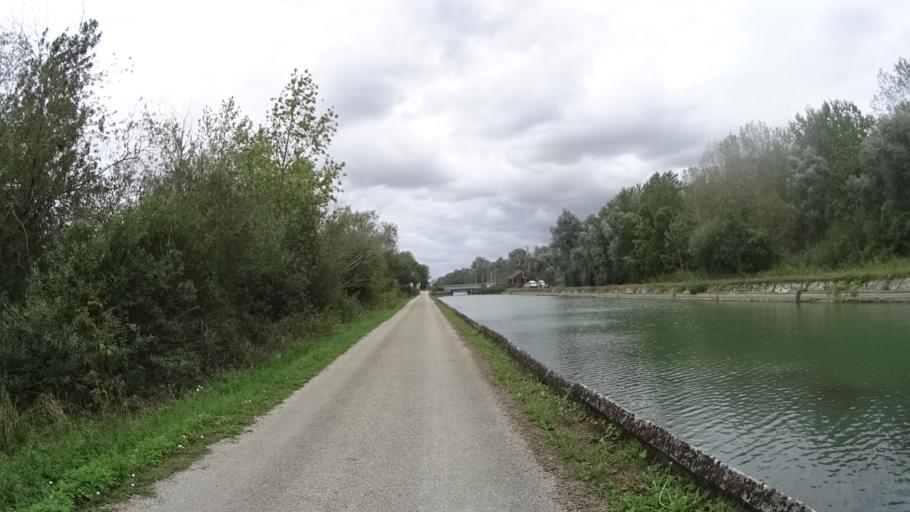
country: FR
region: Picardie
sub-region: Departement de l'Aisne
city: La Fere
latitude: 49.6887
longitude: 3.3667
